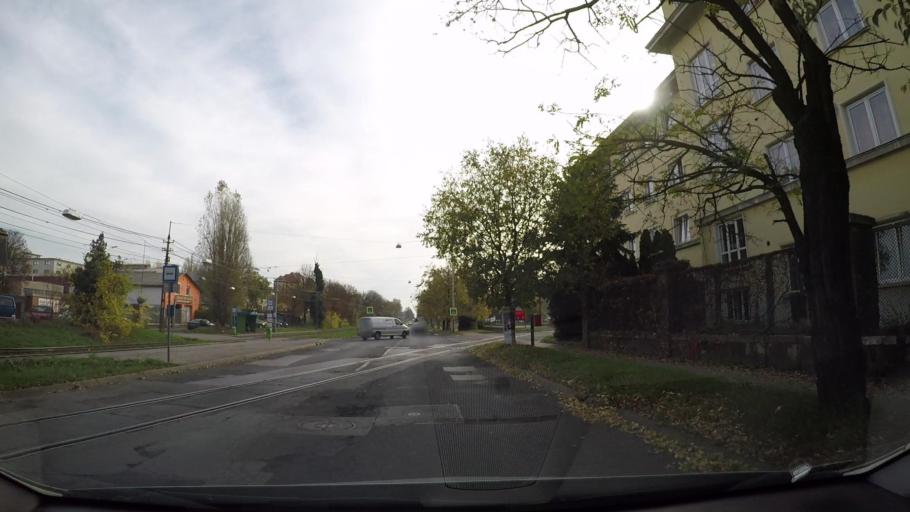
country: HU
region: Budapest
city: Budapest X. keruelet
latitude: 47.4874
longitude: 19.1524
